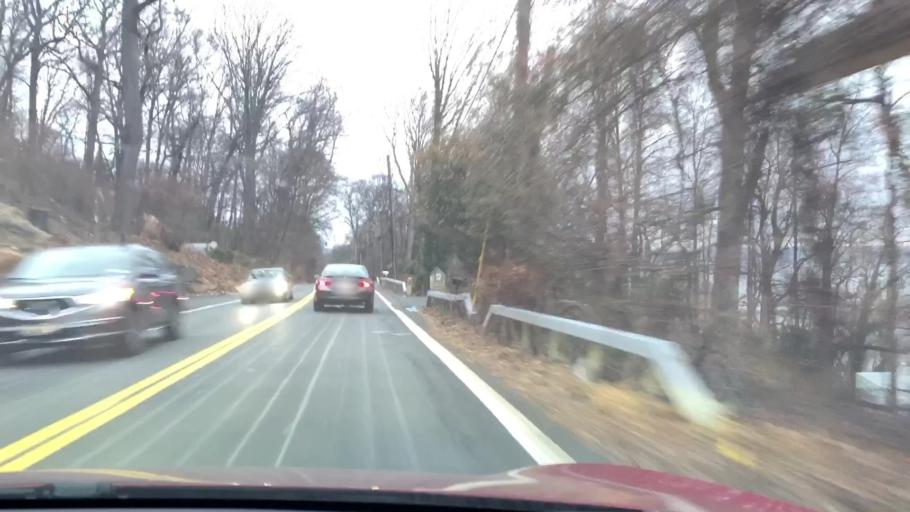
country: US
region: New York
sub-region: Rockland County
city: Piermont
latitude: 41.0596
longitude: -73.9230
